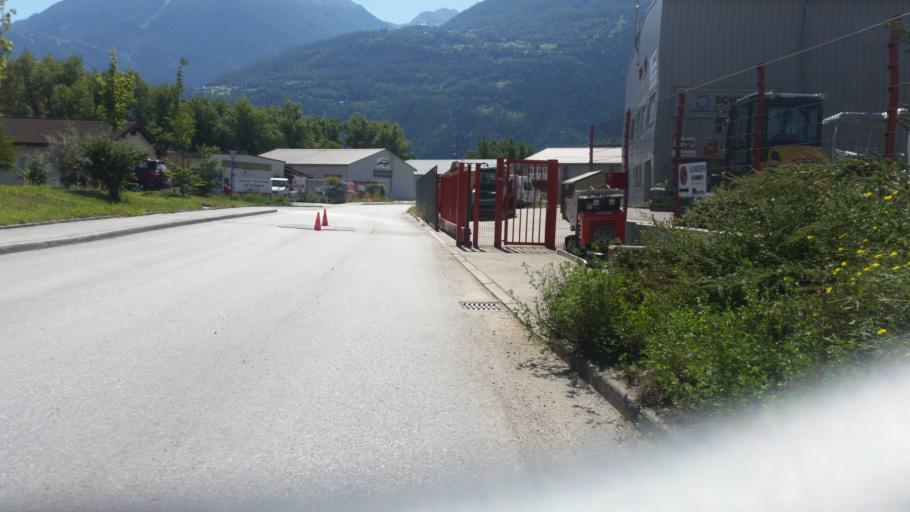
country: CH
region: Valais
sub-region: Leuk District
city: Leuk
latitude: 46.3064
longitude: 7.6601
